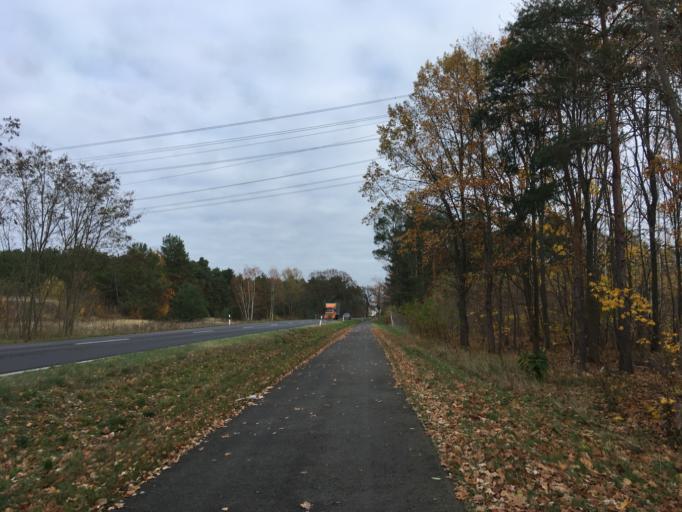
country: DE
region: Brandenburg
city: Tauer
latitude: 51.8884
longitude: 14.4318
